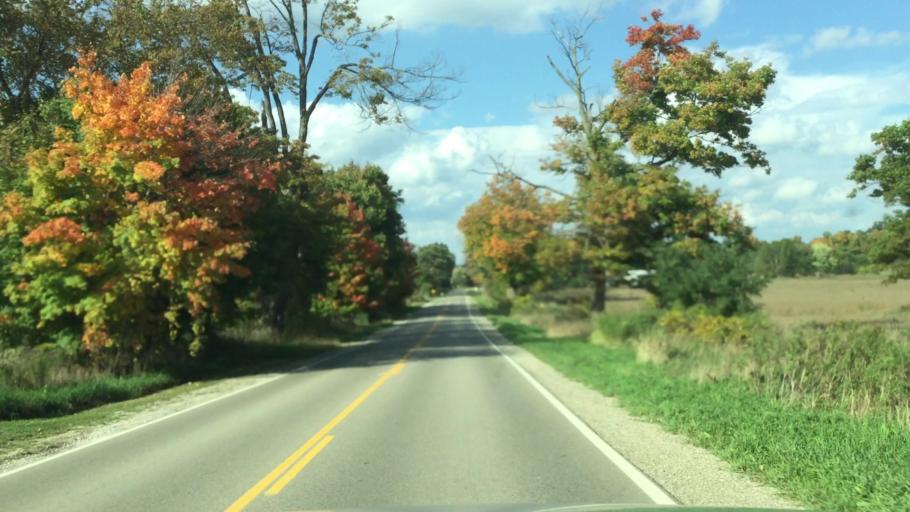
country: US
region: Michigan
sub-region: Genesee County
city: Fenton
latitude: 42.6899
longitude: -83.7029
